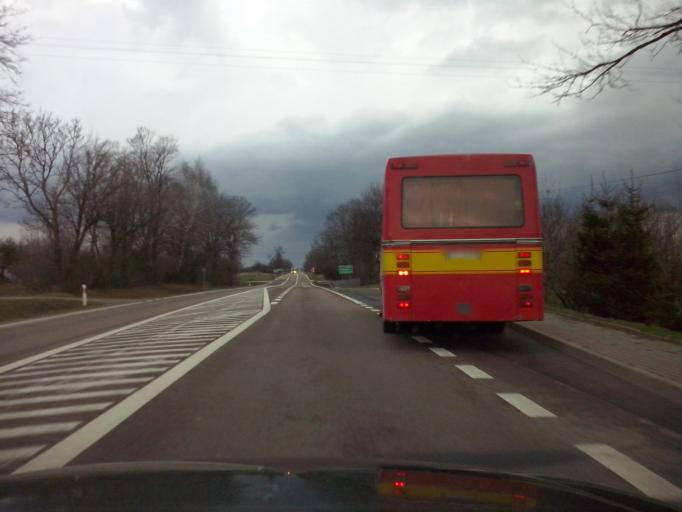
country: PL
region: Lublin Voivodeship
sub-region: Powiat chelmski
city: Rejowiec Fabryczny
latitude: 51.1740
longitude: 23.2693
